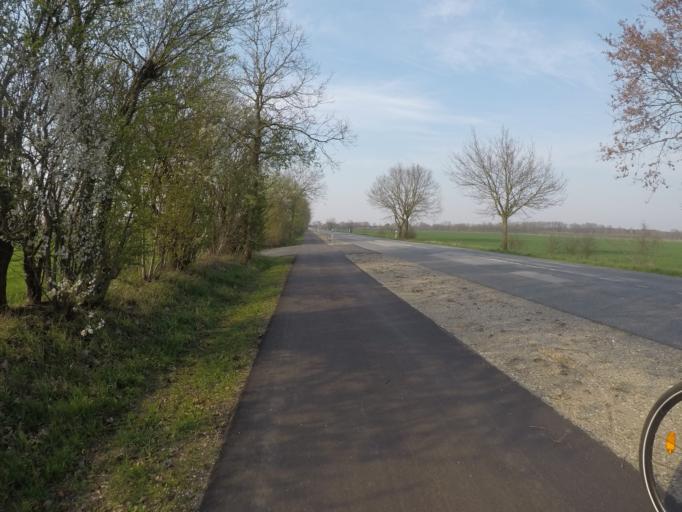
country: DE
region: Schleswig-Holstein
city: Wahlstedt
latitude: 53.9809
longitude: 10.1878
